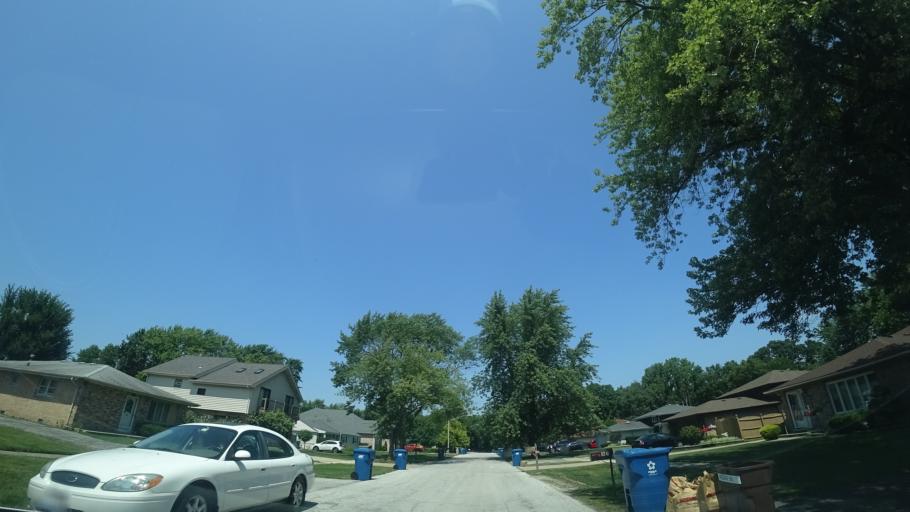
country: US
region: Illinois
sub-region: Cook County
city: Alsip
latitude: 41.6786
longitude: -87.7417
